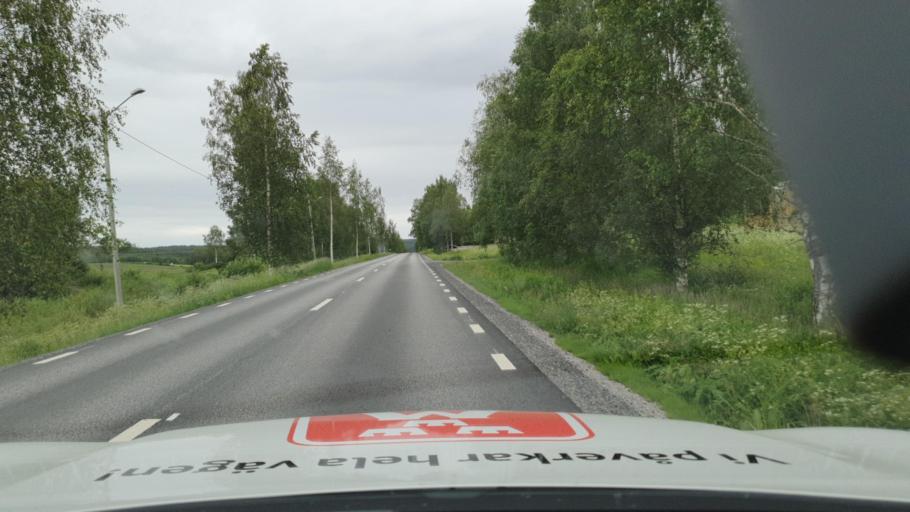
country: SE
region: Vaesterbotten
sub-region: Vannas Kommun
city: Vaennaes
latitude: 63.7513
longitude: 19.6411
